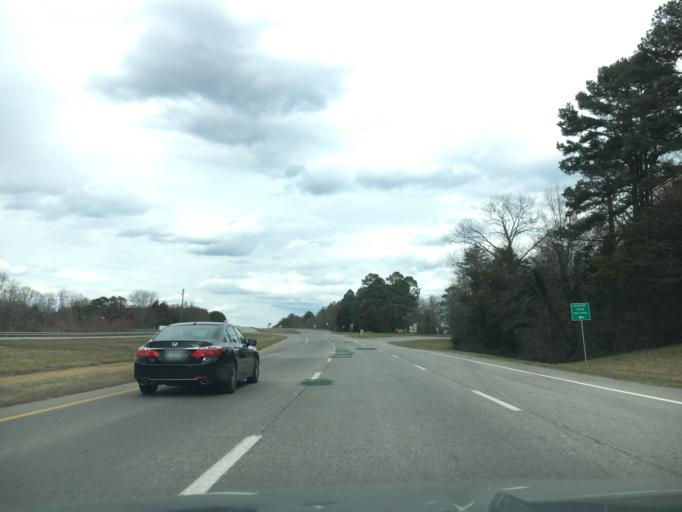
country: US
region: Virginia
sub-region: Mecklenburg County
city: Boydton
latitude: 36.6669
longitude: -78.3980
